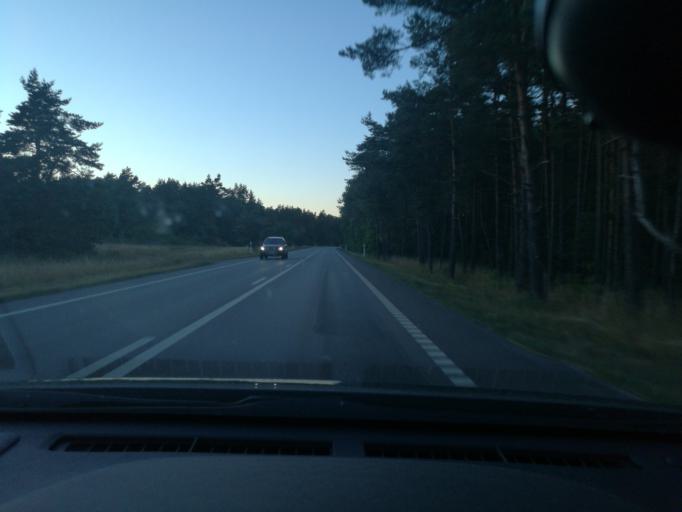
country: SE
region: Kalmar
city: Faerjestaden
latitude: 56.7470
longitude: 16.5481
